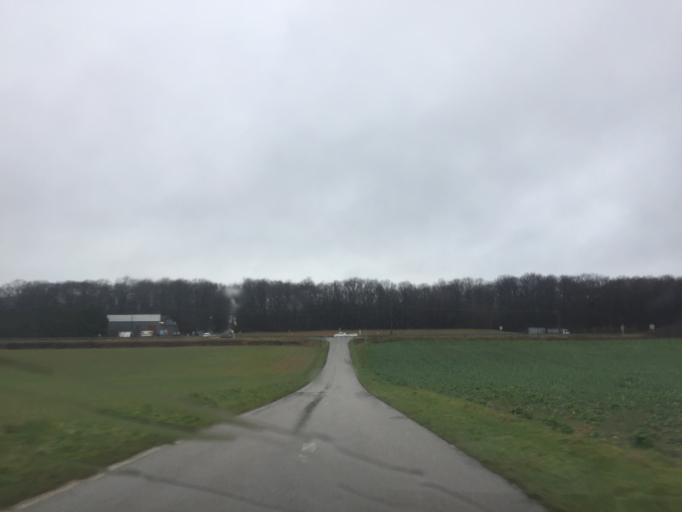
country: FR
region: Franche-Comte
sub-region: Departement du Jura
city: Dole
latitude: 47.1103
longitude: 5.5314
